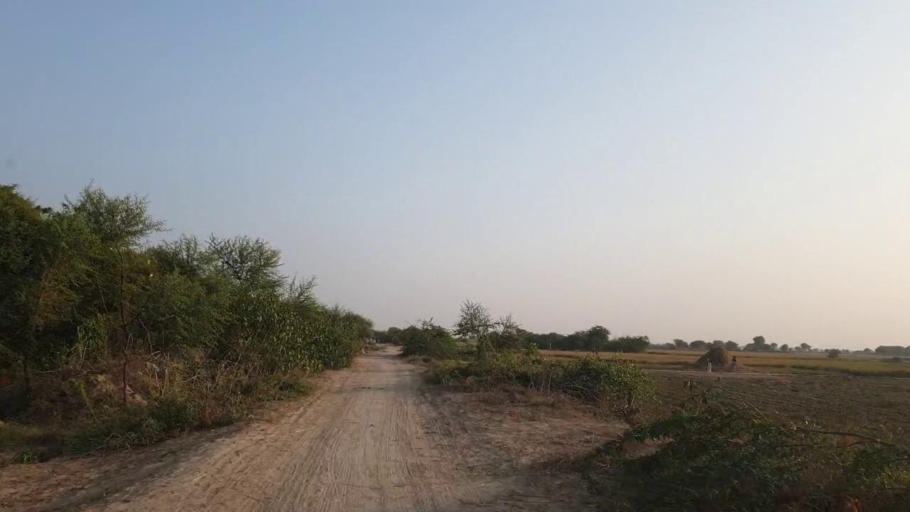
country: PK
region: Sindh
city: Kario
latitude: 24.8608
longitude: 68.6249
